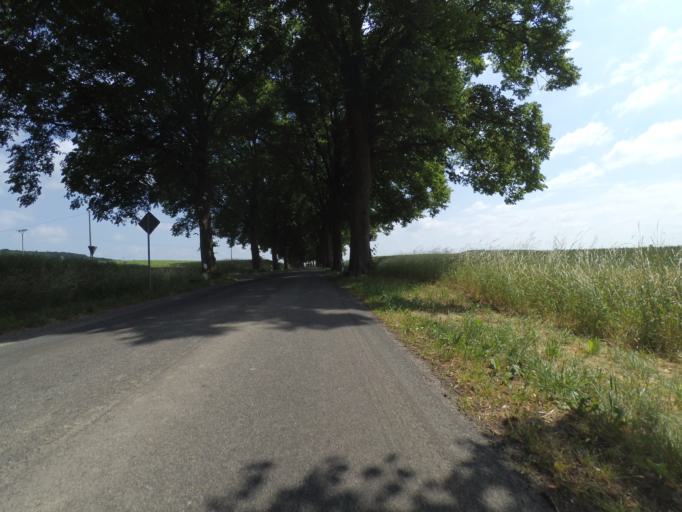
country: DE
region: Mecklenburg-Vorpommern
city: Lubz
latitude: 53.4546
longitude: 12.0487
